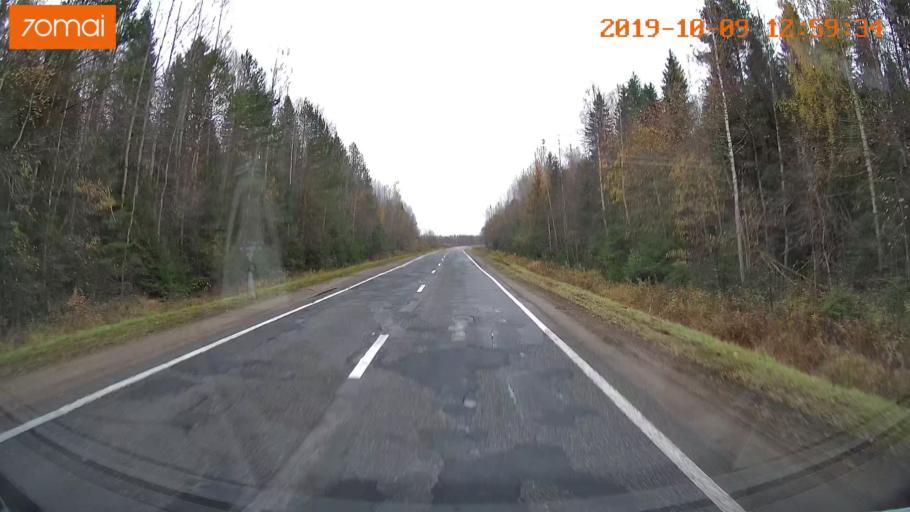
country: RU
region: Jaroslavl
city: Prechistoye
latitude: 58.3829
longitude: 40.4666
